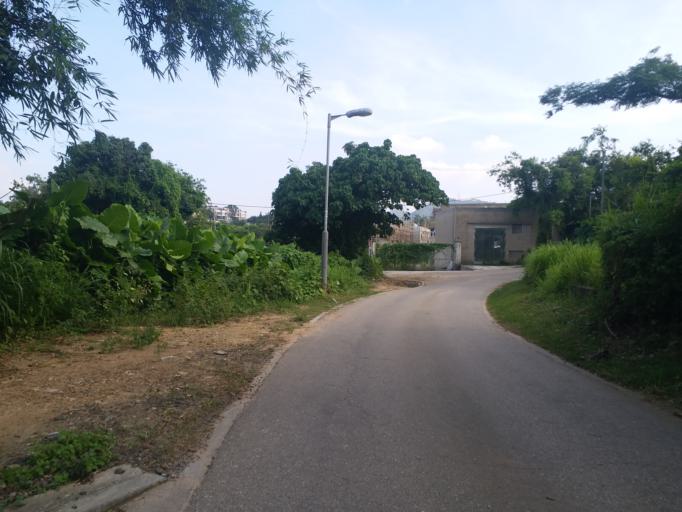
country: HK
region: Yuen Long
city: Yuen Long Kau Hui
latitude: 22.4462
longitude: 114.0120
